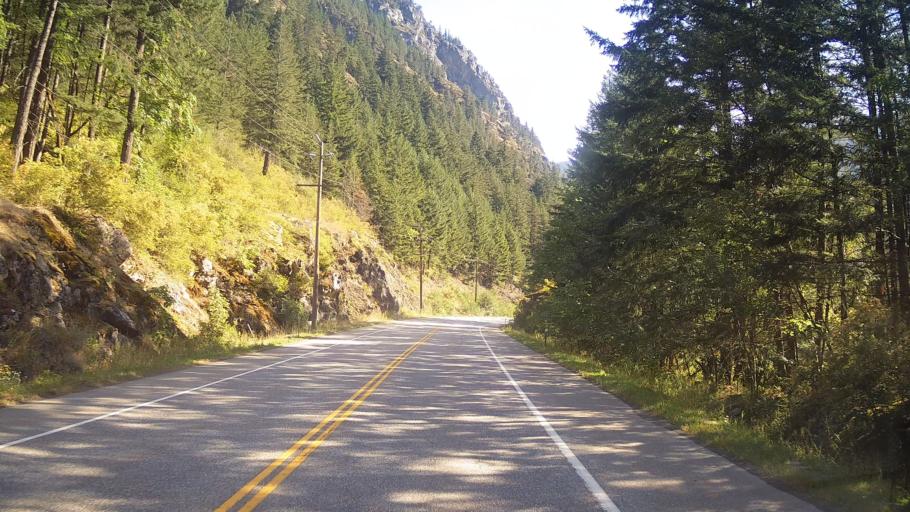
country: CA
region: British Columbia
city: Hope
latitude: 49.6140
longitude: -121.4114
